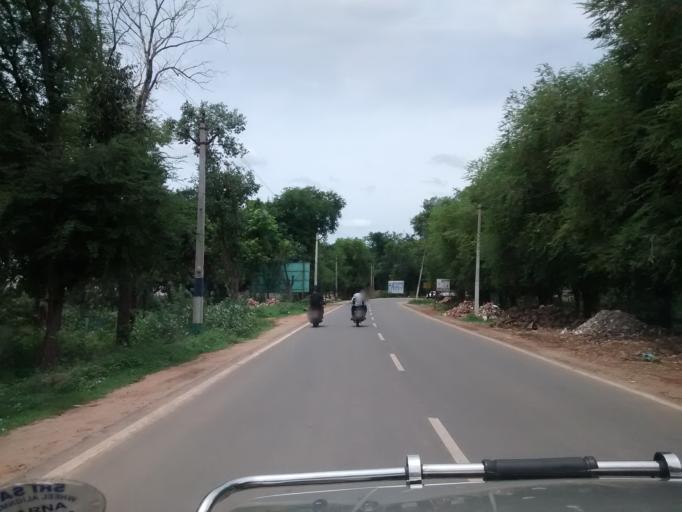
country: IN
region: Andhra Pradesh
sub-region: Chittoor
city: Narasingapuram
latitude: 13.6178
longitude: 79.3631
